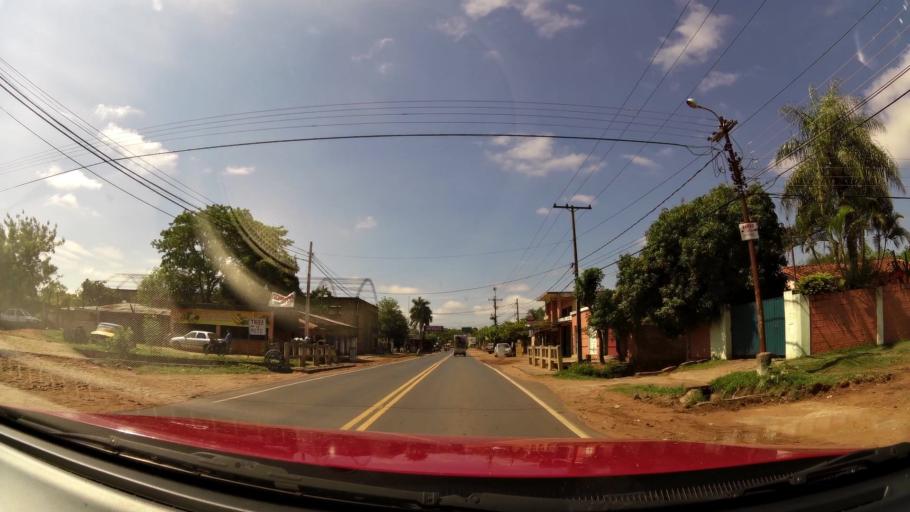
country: PY
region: Central
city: Limpio
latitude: -25.2518
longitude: -57.4894
